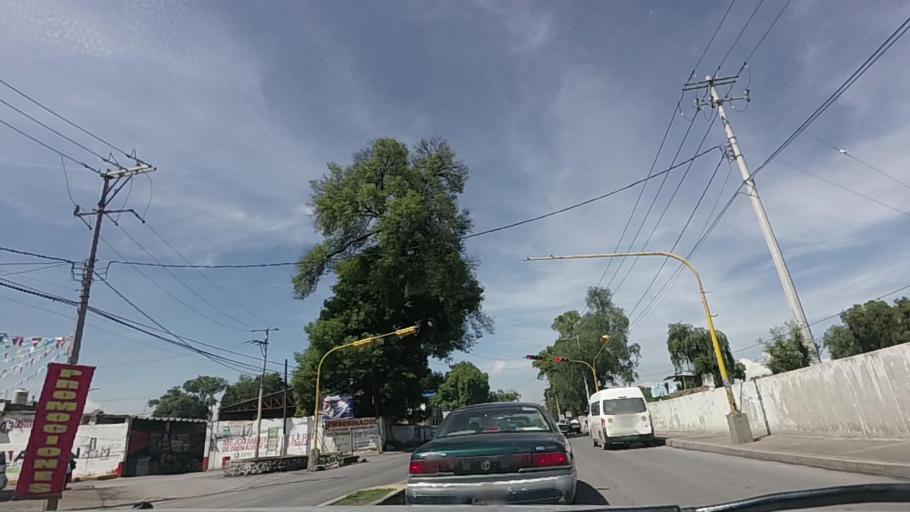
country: MX
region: Mexico
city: Teoloyucan
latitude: 19.7419
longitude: -99.1793
